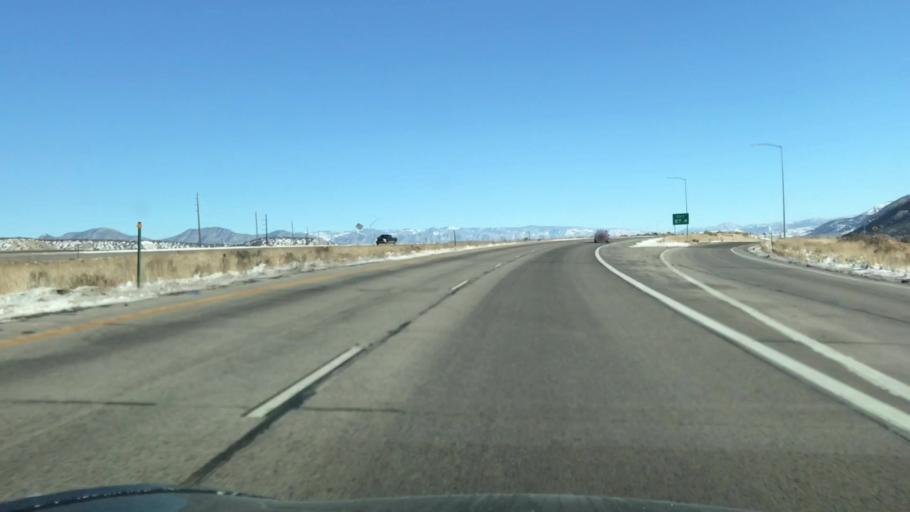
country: US
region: Colorado
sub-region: Garfield County
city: Rifle
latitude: 39.5217
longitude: -107.8500
